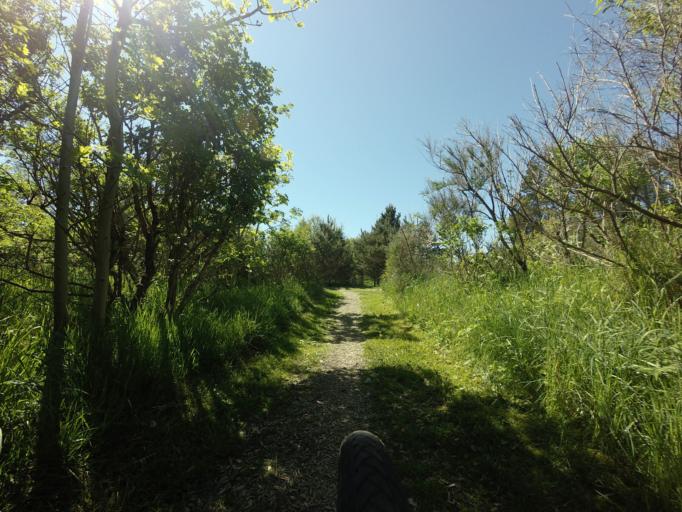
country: DK
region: North Denmark
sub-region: Jammerbugt Kommune
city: Pandrup
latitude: 57.2610
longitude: 9.6190
